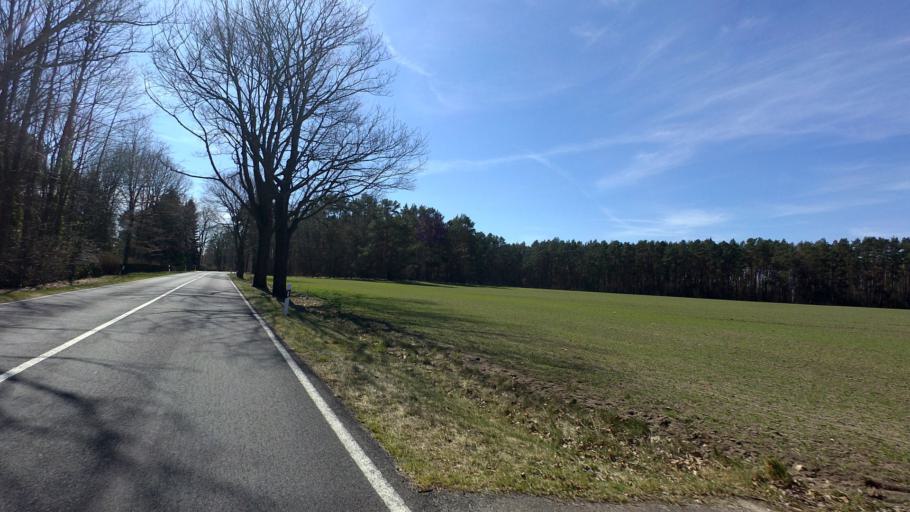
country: DE
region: Brandenburg
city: Teupitz
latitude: 52.1442
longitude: 13.5866
